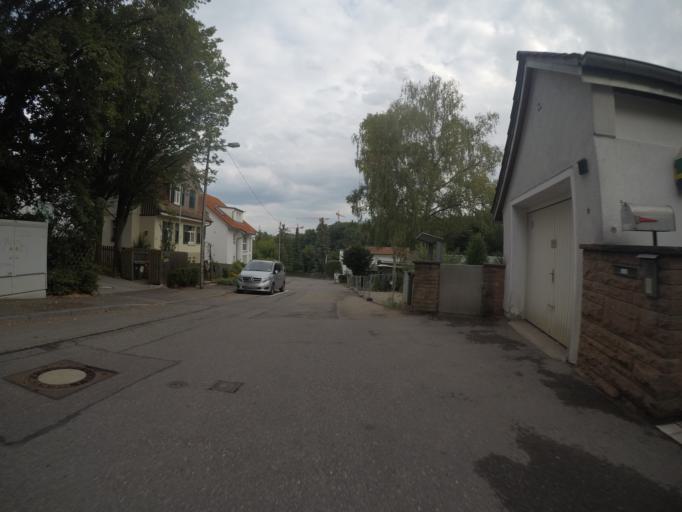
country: DE
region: Baden-Wuerttemberg
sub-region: Regierungsbezirk Stuttgart
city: Ostfildern
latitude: 48.7307
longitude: 9.2038
